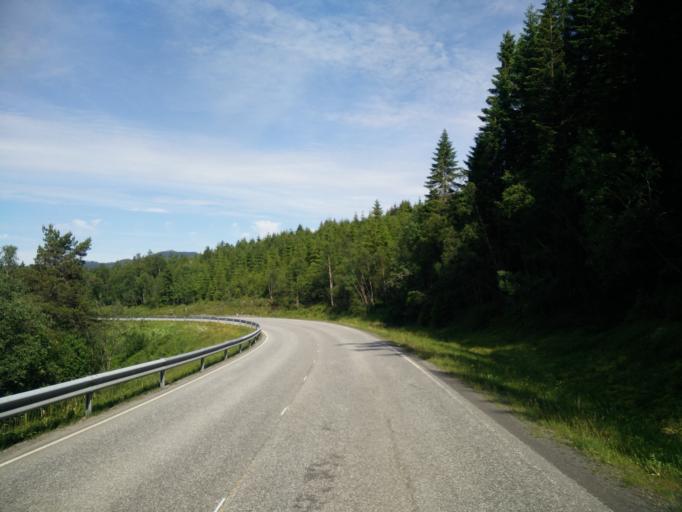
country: NO
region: More og Romsdal
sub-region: Kristiansund
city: Rensvik
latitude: 63.0262
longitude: 8.0215
